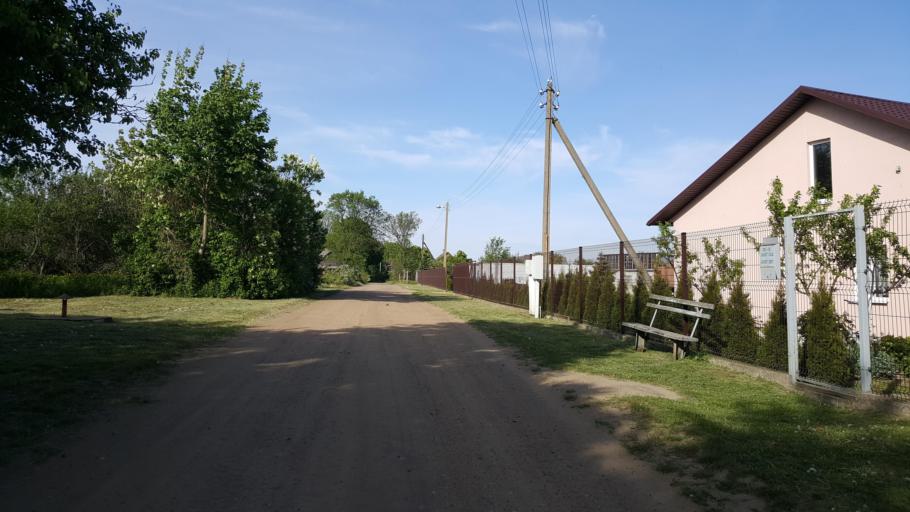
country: BY
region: Brest
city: Kamyanyets
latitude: 52.3615
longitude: 23.8679
